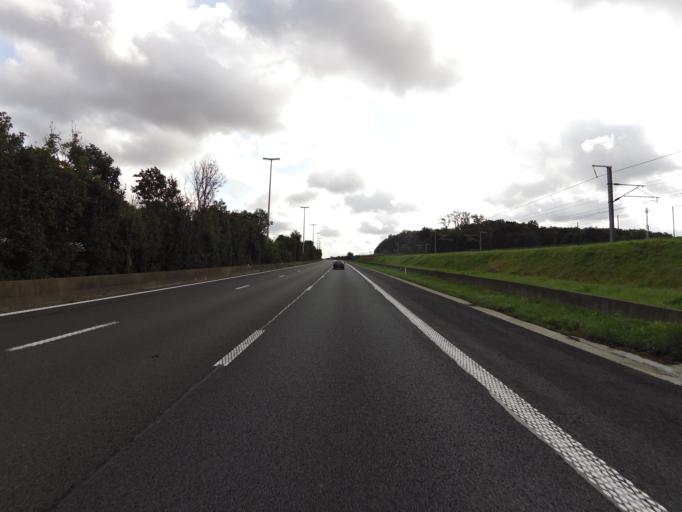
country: BE
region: Wallonia
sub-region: Province de Liege
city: Lincent
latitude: 50.7193
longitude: 5.0039
